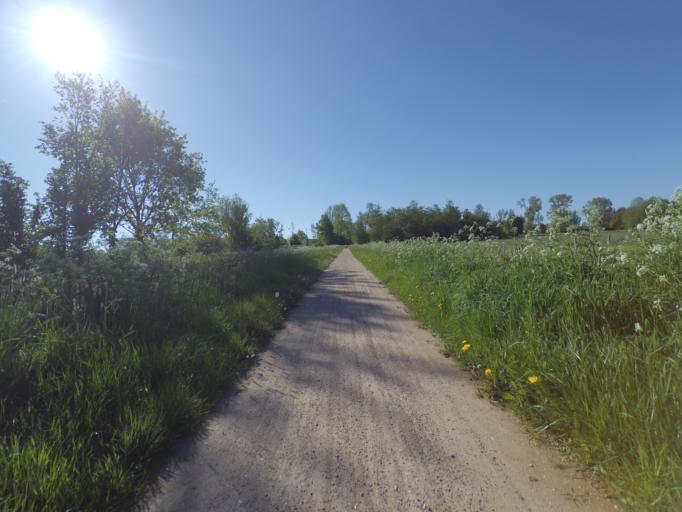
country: NL
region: Gelderland
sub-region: Gemeente Voorst
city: Wilp
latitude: 52.2084
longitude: 6.1235
